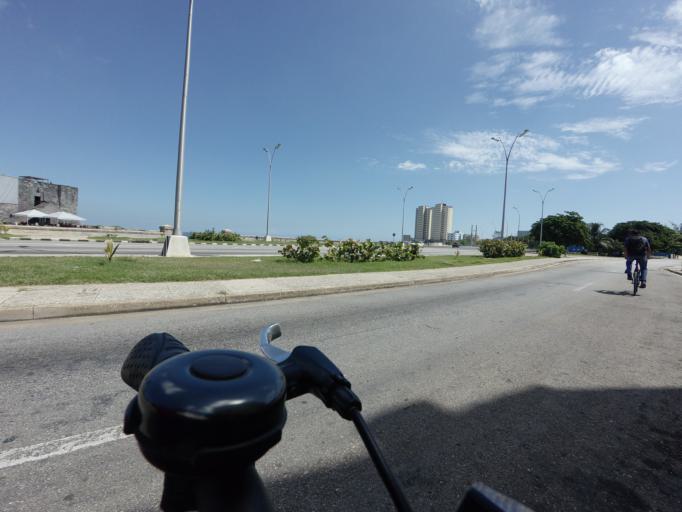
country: CU
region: La Habana
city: Havana
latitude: 23.1316
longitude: -82.4086
